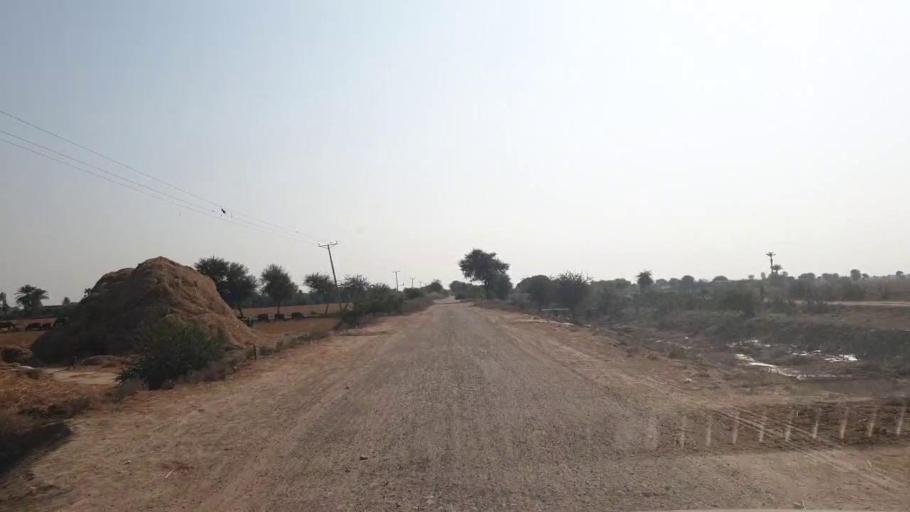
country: PK
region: Sindh
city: Kario
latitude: 24.9046
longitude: 68.6487
